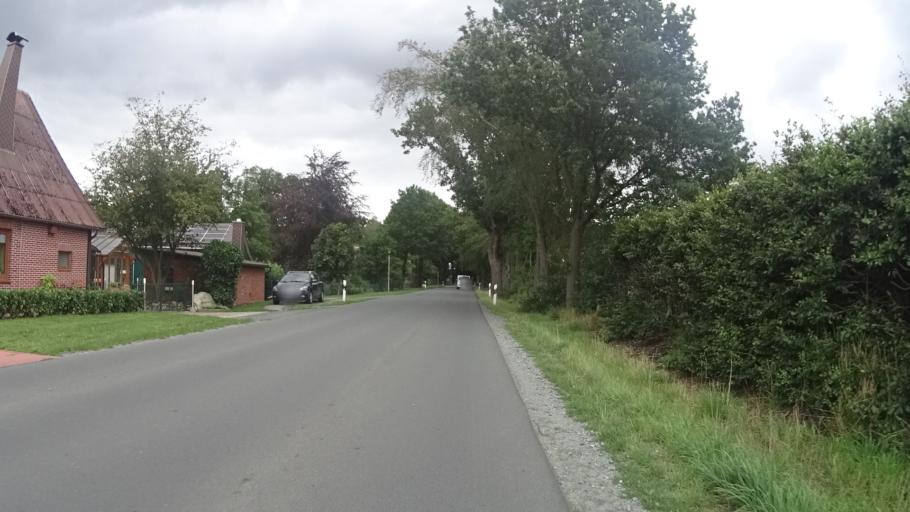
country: DE
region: Lower Saxony
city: Kuhrstedt
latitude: 53.5848
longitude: 8.8016
